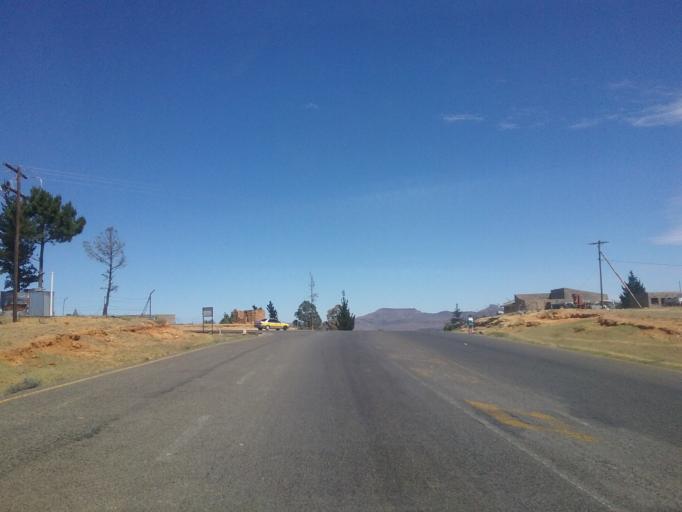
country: LS
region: Mohale's Hoek District
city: Mohale's Hoek
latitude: -30.2025
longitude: 27.4208
